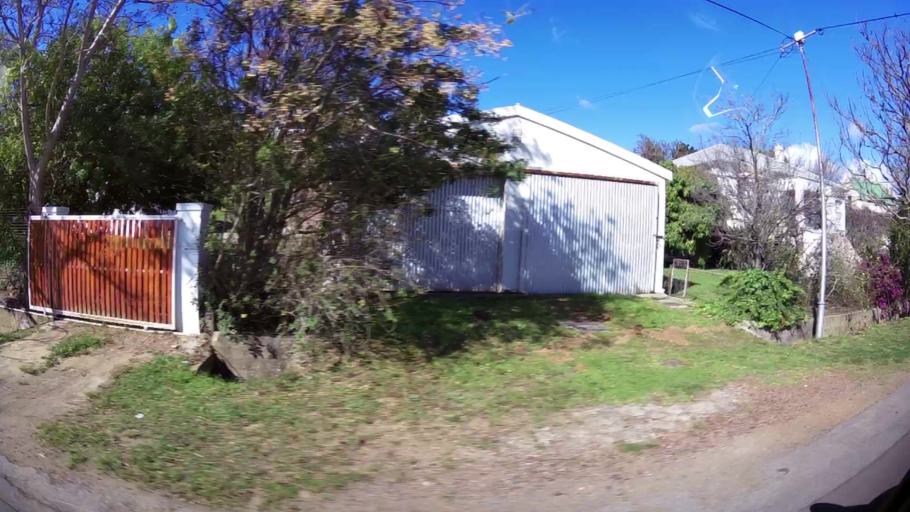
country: ZA
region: Western Cape
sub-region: Overberg District Municipality
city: Swellendam
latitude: -34.0235
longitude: 20.4474
